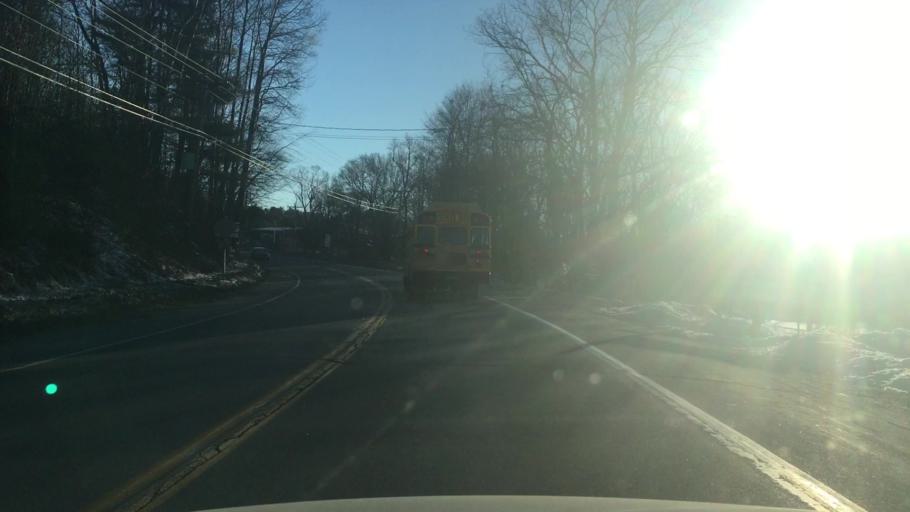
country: US
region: Maine
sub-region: Somerset County
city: Norridgewock
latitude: 44.7150
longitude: -69.7887
